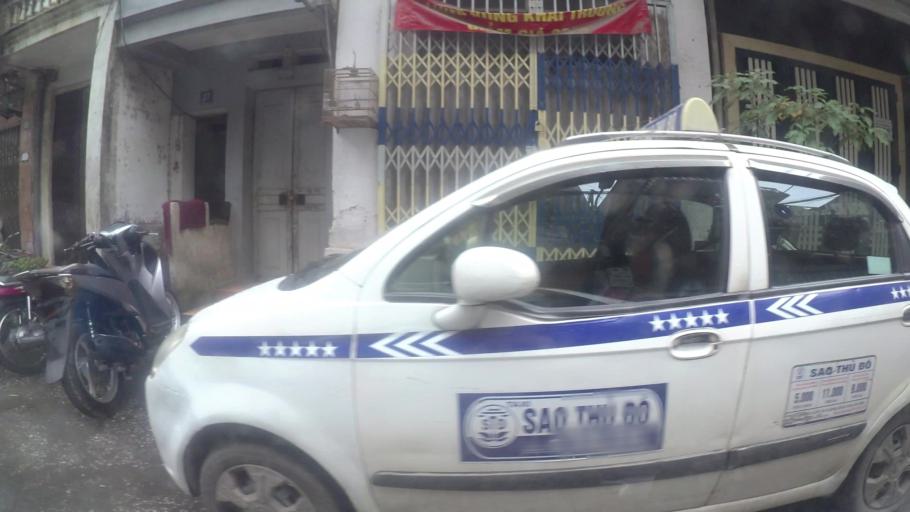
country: VN
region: Ha Noi
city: Hoan Kiem
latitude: 21.0388
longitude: 105.8545
